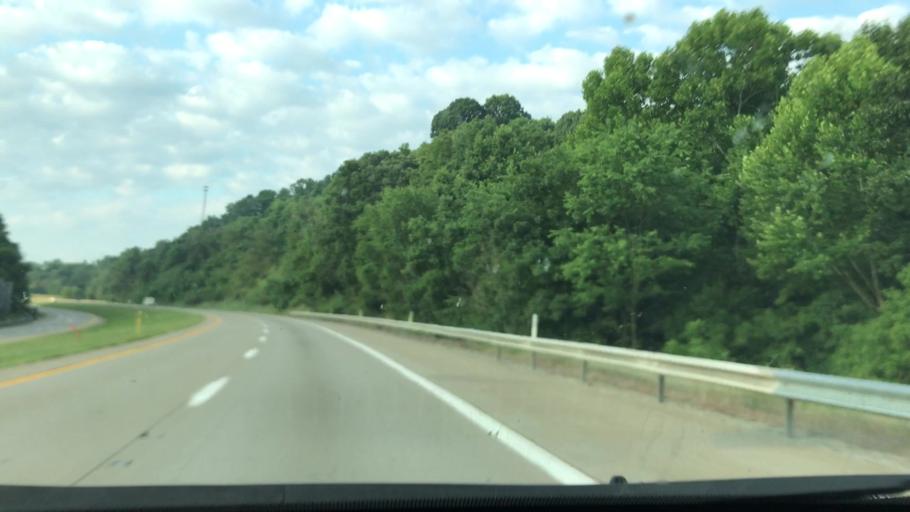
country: US
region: Pennsylvania
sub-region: Greene County
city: Waynesburg
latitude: 39.9401
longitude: -80.1698
